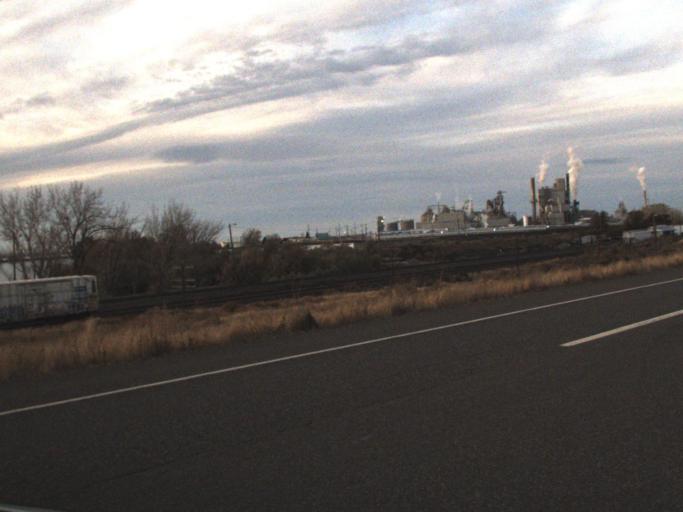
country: US
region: Washington
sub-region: Benton County
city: Finley
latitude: 46.0957
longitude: -118.9118
